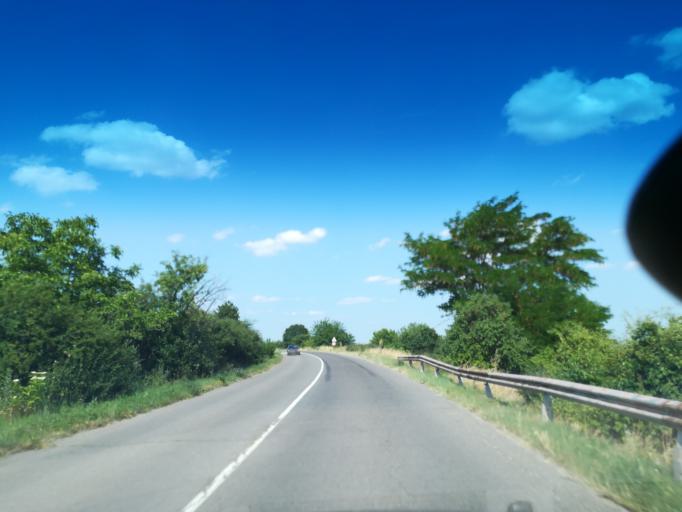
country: BG
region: Stara Zagora
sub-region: Obshtina Chirpan
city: Chirpan
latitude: 42.2187
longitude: 25.3813
